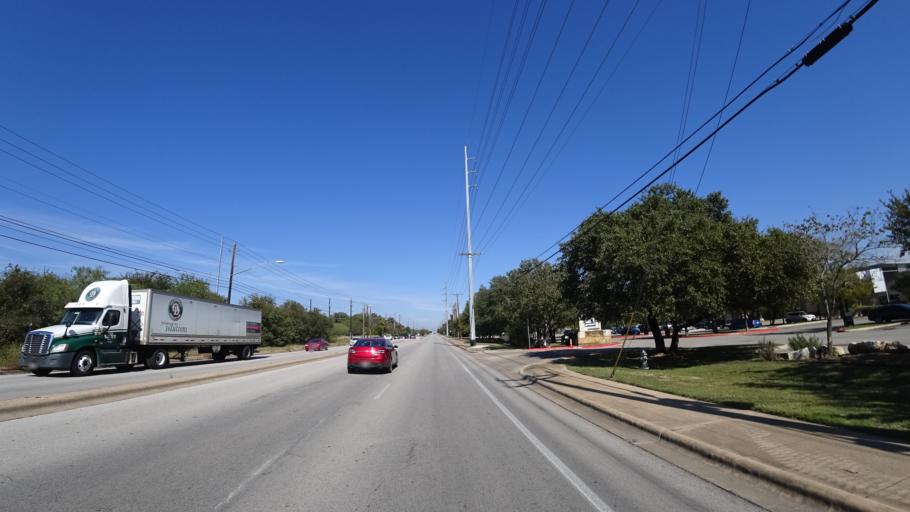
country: US
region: Texas
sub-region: Travis County
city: Shady Hollow
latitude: 30.1860
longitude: -97.8481
